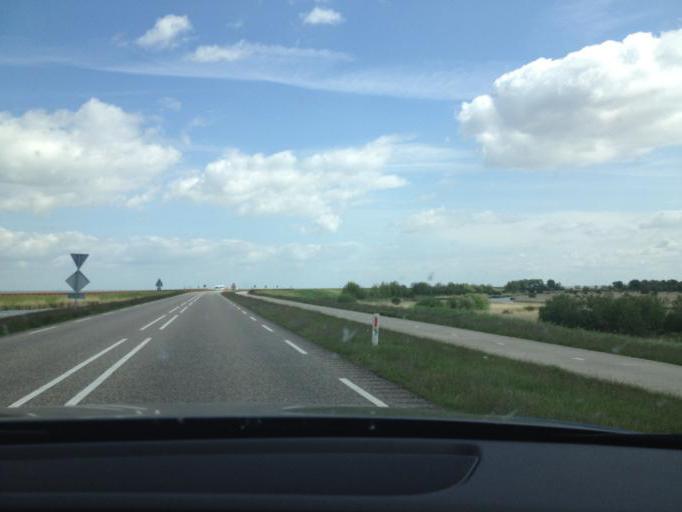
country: NL
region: Flevoland
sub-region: Gemeente Almere
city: Almere Stad
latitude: 52.4237
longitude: 5.2316
